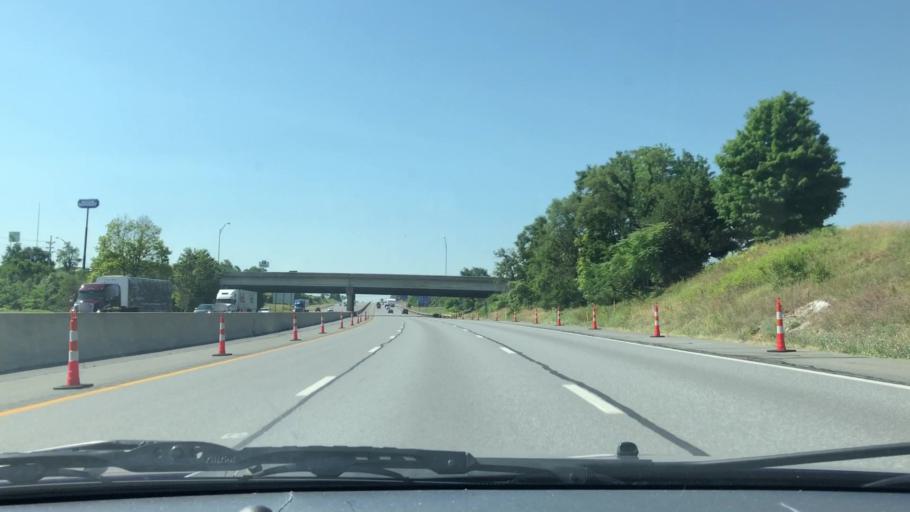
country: US
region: West Virginia
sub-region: Berkeley County
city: Martinsburg
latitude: 39.4668
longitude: -77.9903
